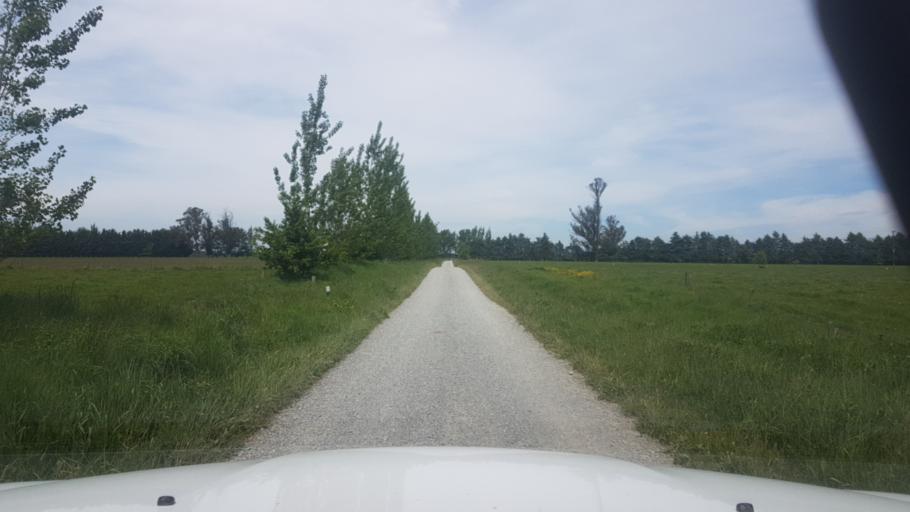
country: NZ
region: Canterbury
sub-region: Timaru District
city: Pleasant Point
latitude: -44.1995
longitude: 171.0904
